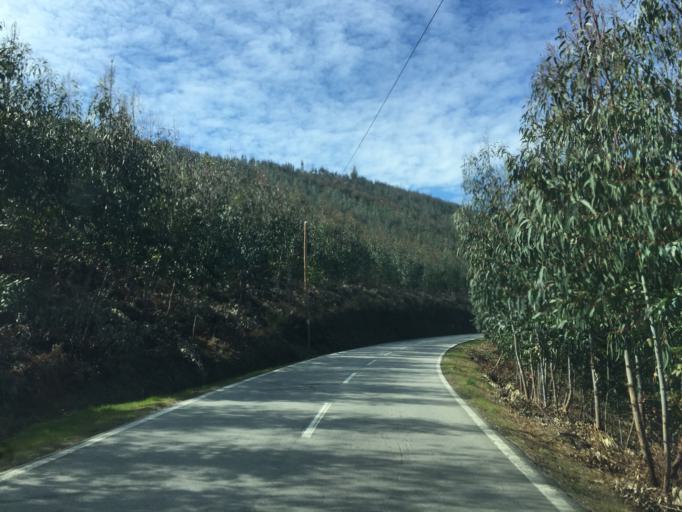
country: PT
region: Aveiro
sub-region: Arouca
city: Arouca
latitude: 40.9588
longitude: -8.2009
